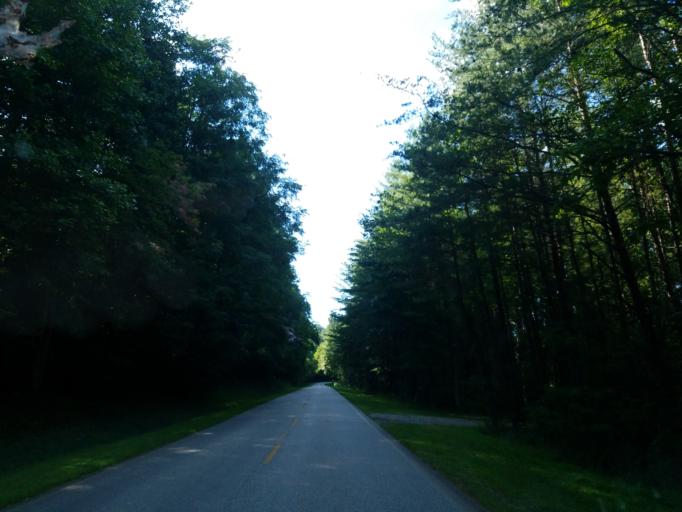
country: US
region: Georgia
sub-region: Fannin County
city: Blue Ridge
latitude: 34.7191
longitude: -84.2320
